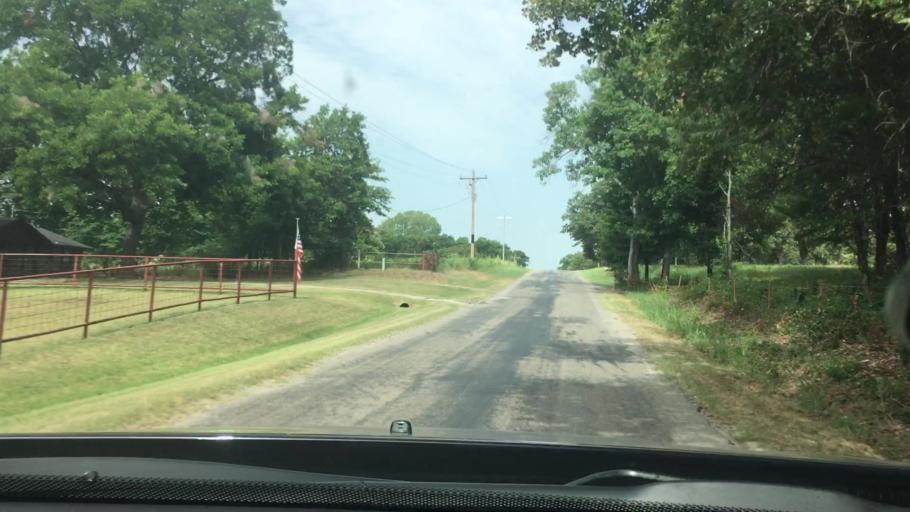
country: US
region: Oklahoma
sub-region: Garvin County
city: Pauls Valley
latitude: 34.7969
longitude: -97.1914
